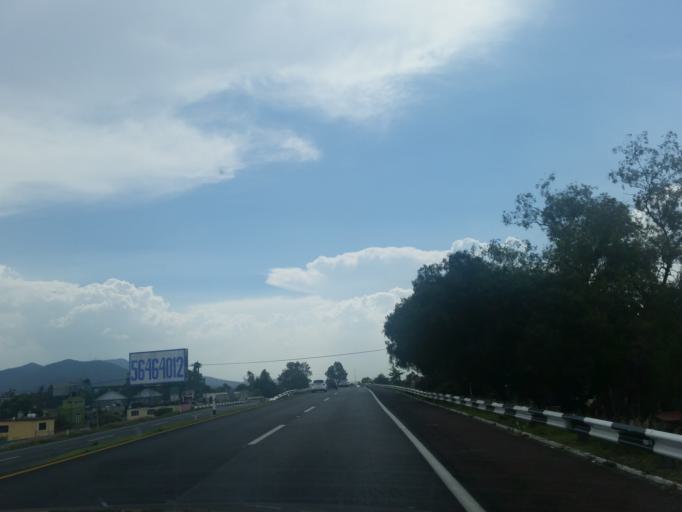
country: MX
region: Mexico
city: Santo Tomas Chiconautla
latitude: 19.6233
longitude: -99.0001
